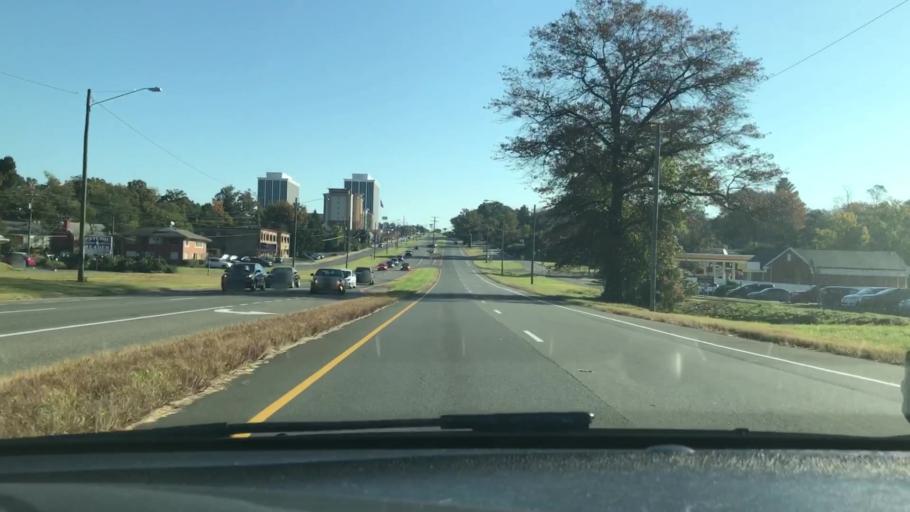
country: US
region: Virginia
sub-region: City of Falls Church
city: Falls Church
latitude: 38.8707
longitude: -77.1683
